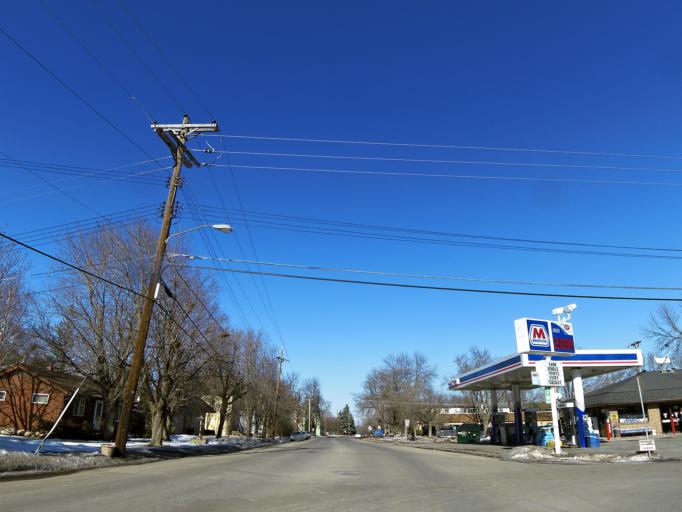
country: US
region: Minnesota
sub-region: Washington County
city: Stillwater
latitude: 45.0646
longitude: -92.8205
